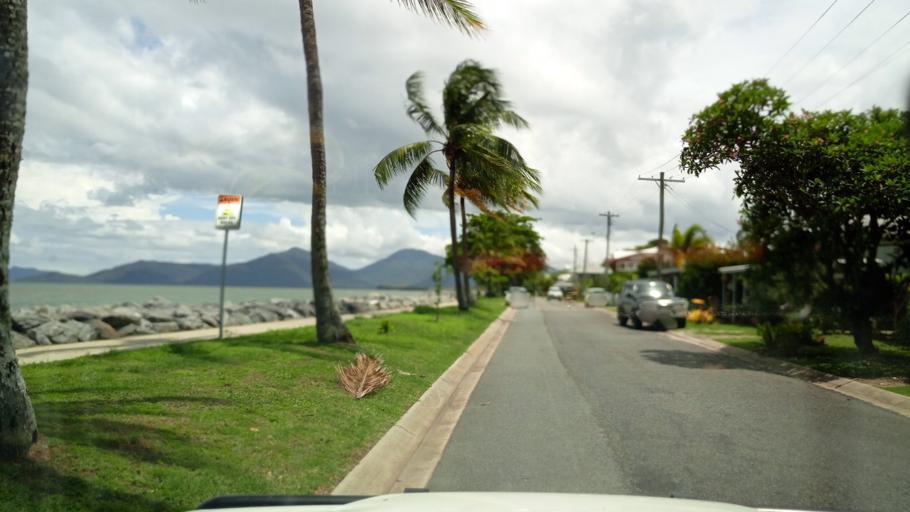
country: AU
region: Queensland
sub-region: Cairns
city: Yorkeys Knob
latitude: -16.8502
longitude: 145.7489
